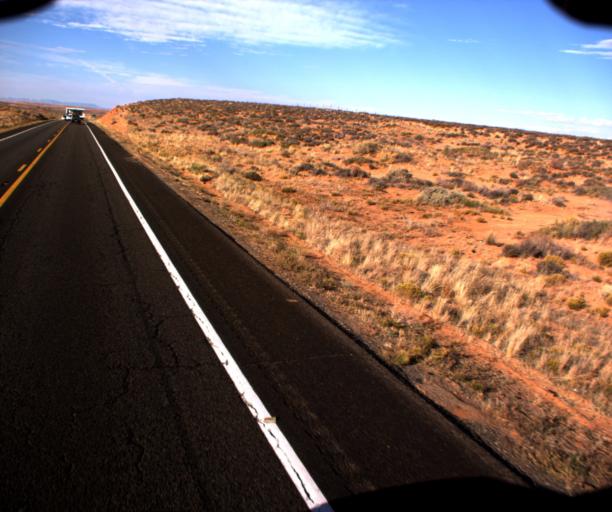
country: US
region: Arizona
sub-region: Apache County
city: Many Farms
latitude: 36.9324
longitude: -109.5691
